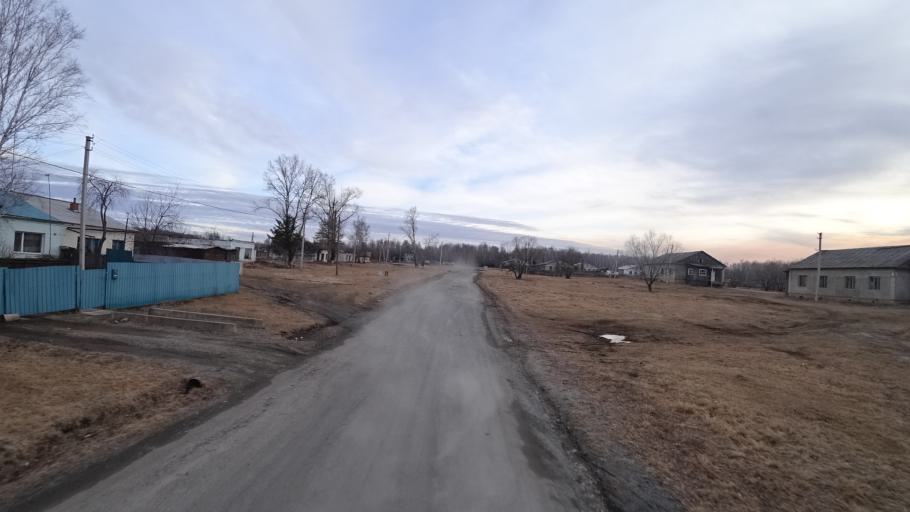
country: RU
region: Amur
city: Bureya
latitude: 50.0172
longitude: 129.7681
